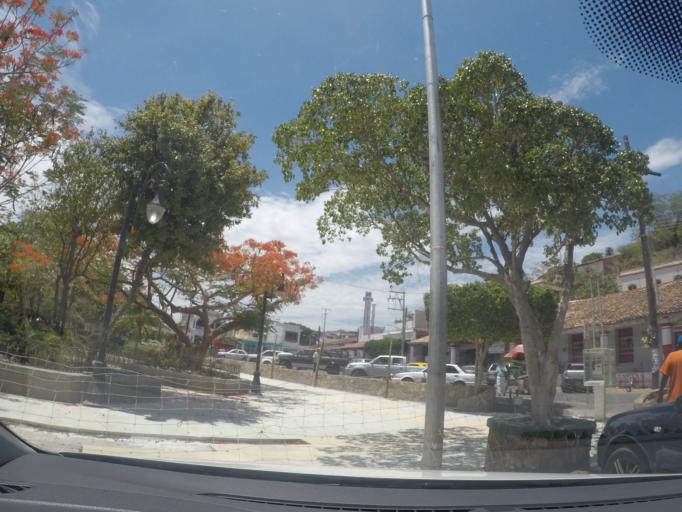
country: MX
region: Oaxaca
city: San Blas Atempa
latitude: 16.3323
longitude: -95.2319
